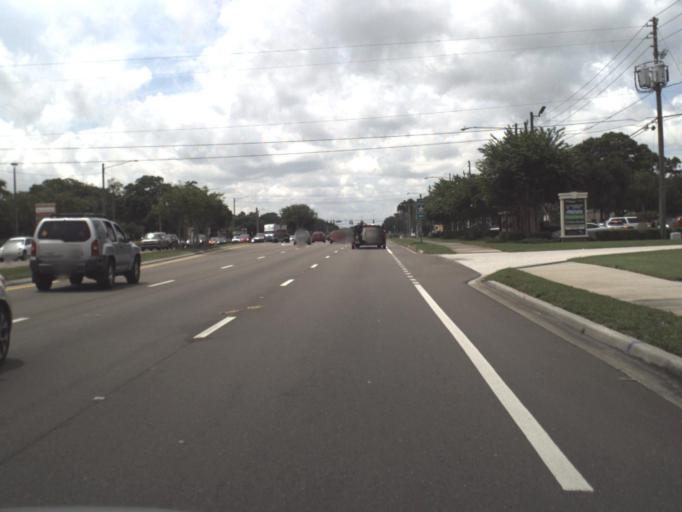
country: US
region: Florida
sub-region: Pinellas County
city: Safety Harbor
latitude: 28.0149
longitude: -82.7091
